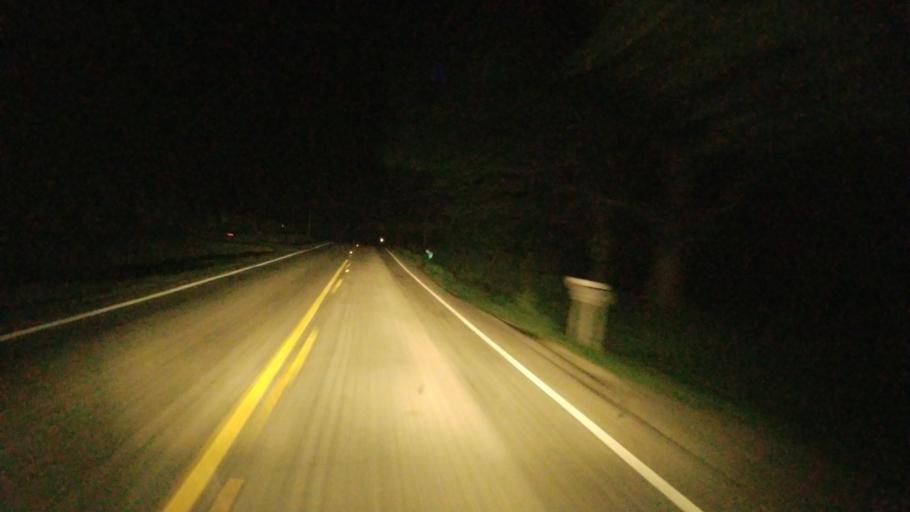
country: US
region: Ohio
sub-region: Ashtabula County
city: Orwell
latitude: 41.5462
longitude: -80.7662
